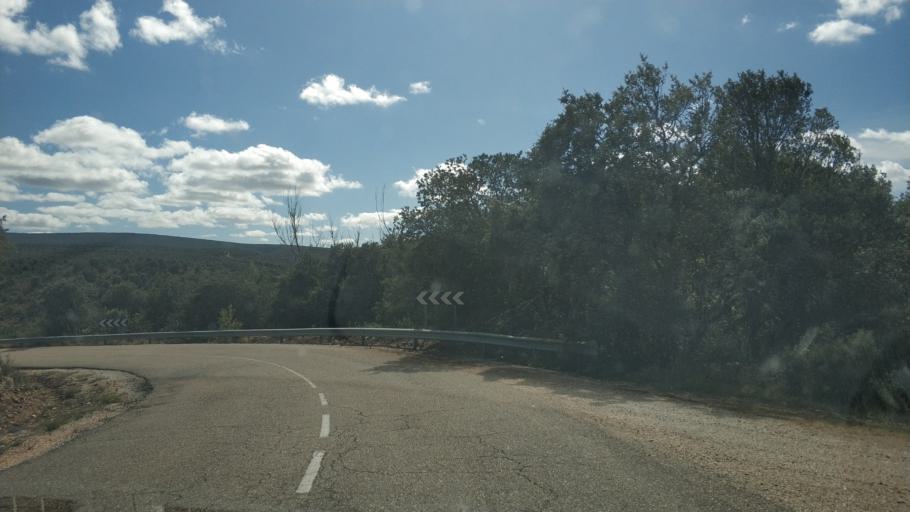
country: ES
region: Castille and Leon
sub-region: Provincia de Burgos
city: Retuerta
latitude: 42.0424
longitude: -3.4949
